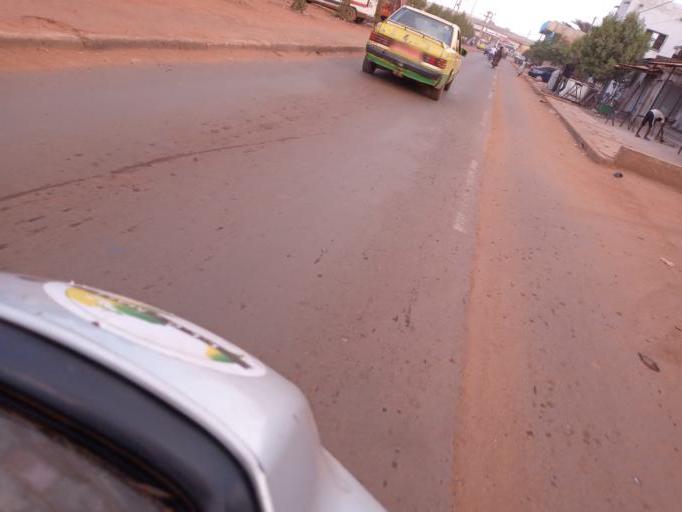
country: ML
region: Bamako
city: Bamako
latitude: 12.5975
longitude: -7.9396
